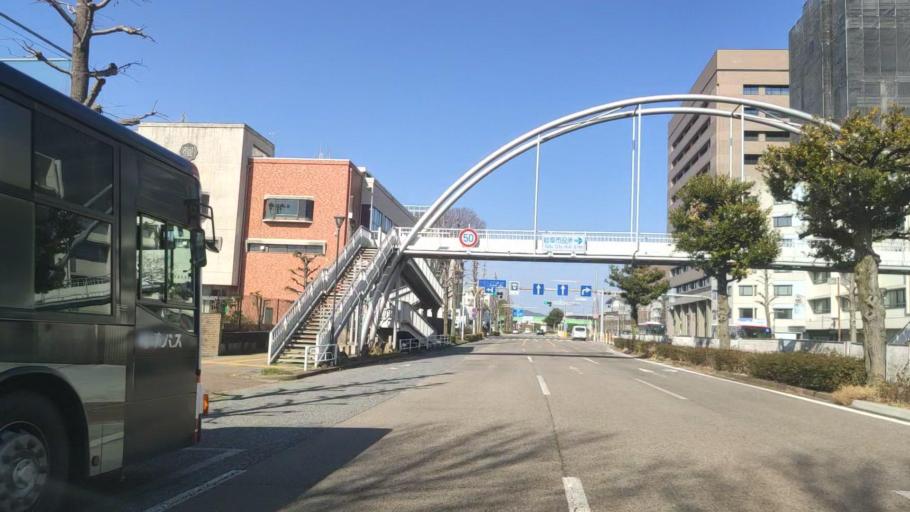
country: JP
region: Gifu
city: Gifu-shi
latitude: 35.4231
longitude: 136.7581
